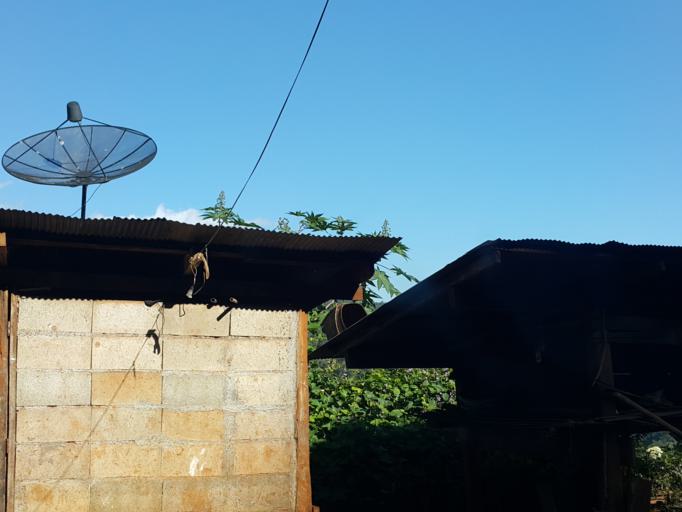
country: TH
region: Chiang Mai
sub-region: Amphoe Chiang Dao
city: Chiang Dao
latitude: 19.5260
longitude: 98.8651
